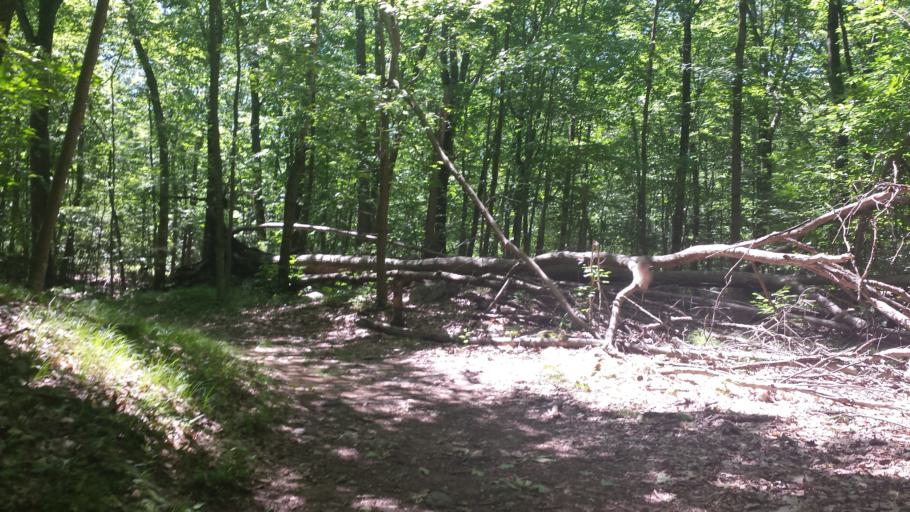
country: US
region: New York
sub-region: Westchester County
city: Pound Ridge
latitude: 41.2326
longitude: -73.5942
